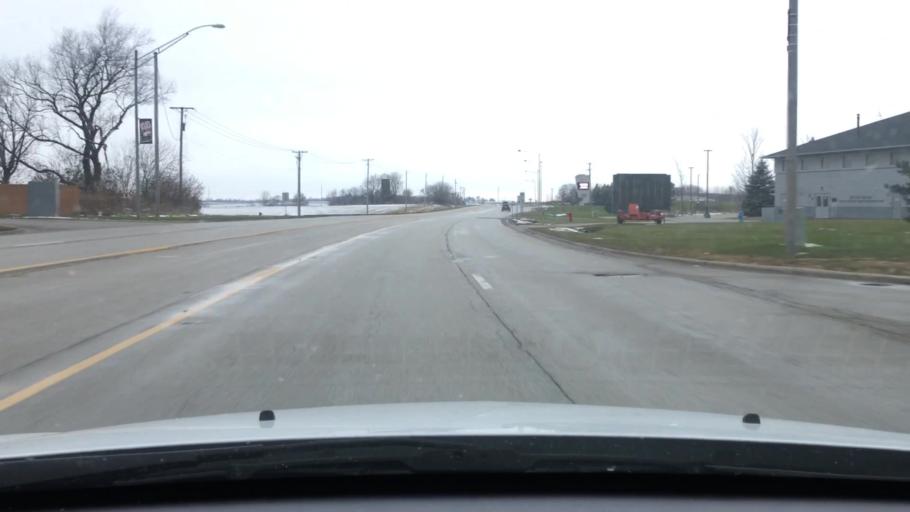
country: US
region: Illinois
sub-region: DeKalb County
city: DeKalb
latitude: 41.9310
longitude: -88.7819
